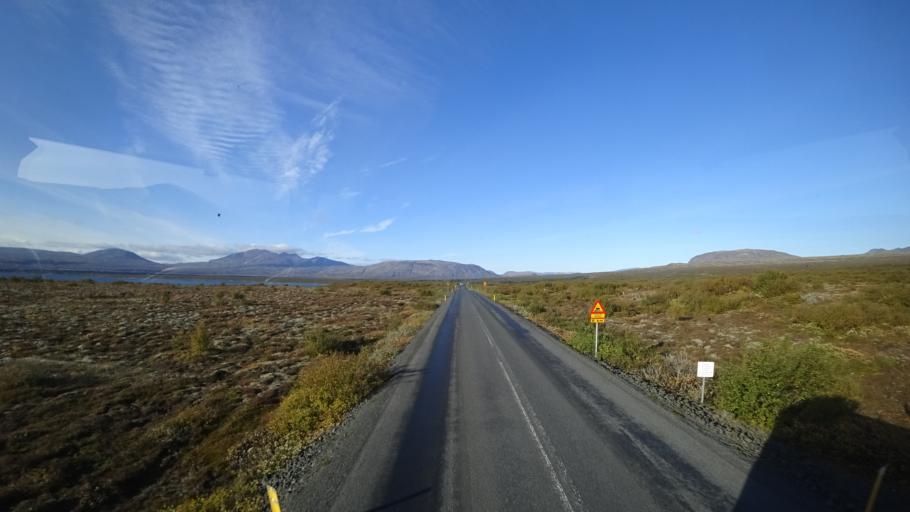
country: IS
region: South
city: Hveragerdi
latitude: 64.2257
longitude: -21.0531
